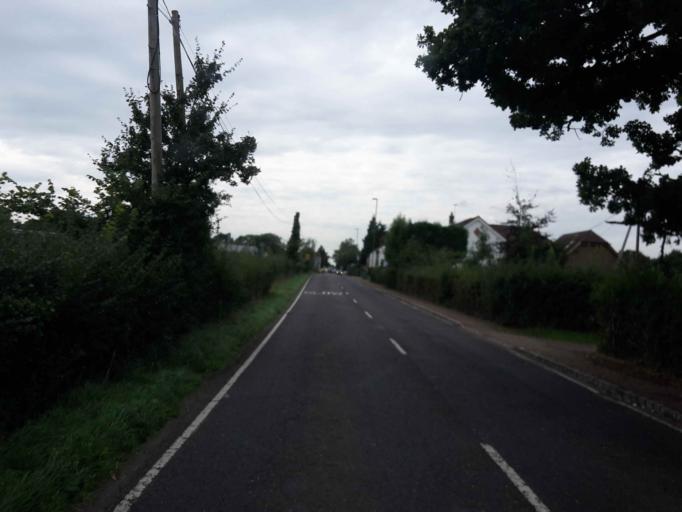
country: GB
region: England
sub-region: West Sussex
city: Billingshurst
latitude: 51.0472
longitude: -0.4334
